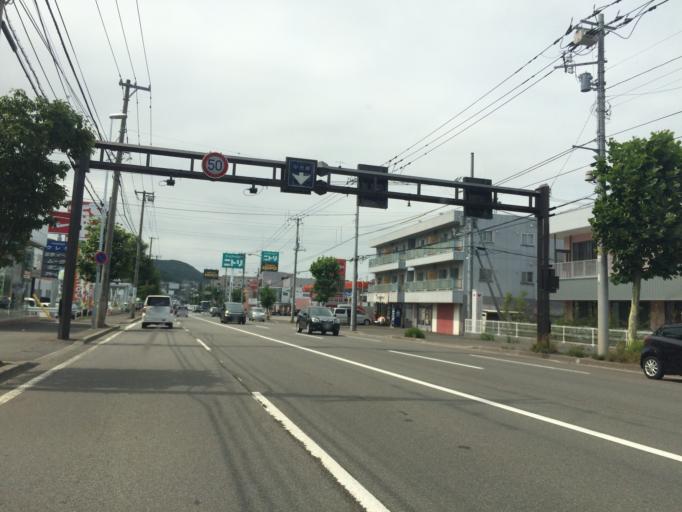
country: JP
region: Hokkaido
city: Sapporo
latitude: 43.0953
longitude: 141.2610
